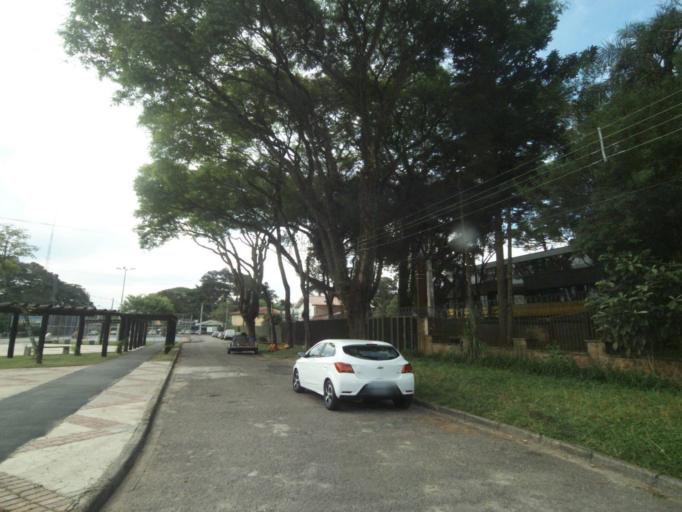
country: BR
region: Parana
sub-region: Curitiba
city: Curitiba
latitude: -25.4325
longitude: -49.2383
